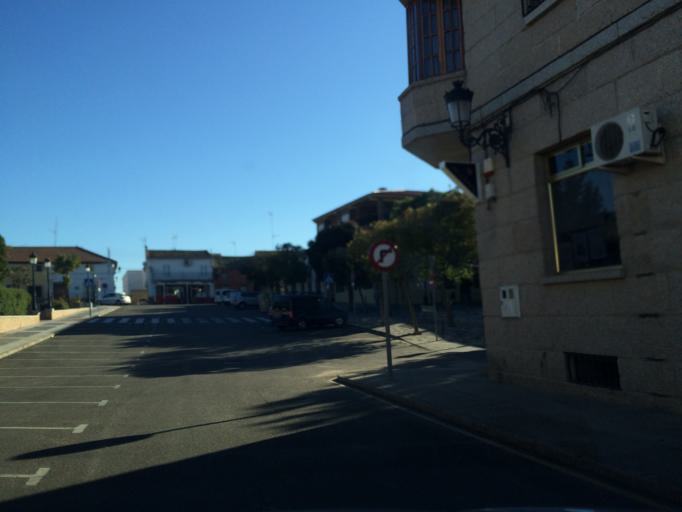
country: ES
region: Castille-La Mancha
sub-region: Province of Toledo
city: Carranque
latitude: 40.1706
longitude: -3.8997
